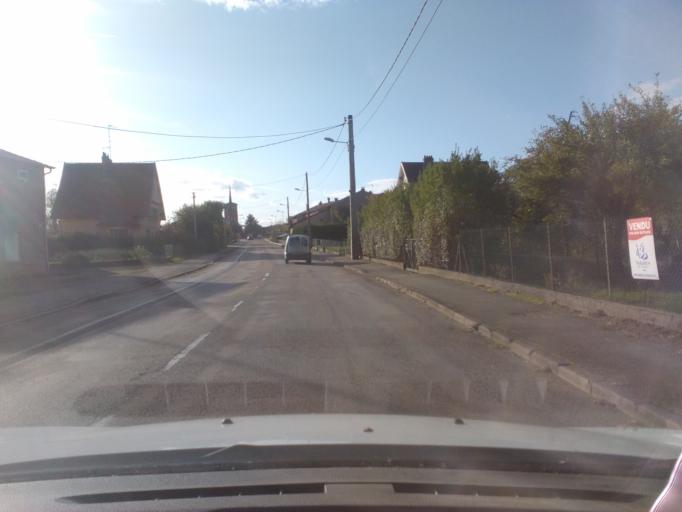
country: FR
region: Lorraine
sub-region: Departement des Vosges
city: Jeanmenil
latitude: 48.3355
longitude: 6.6930
